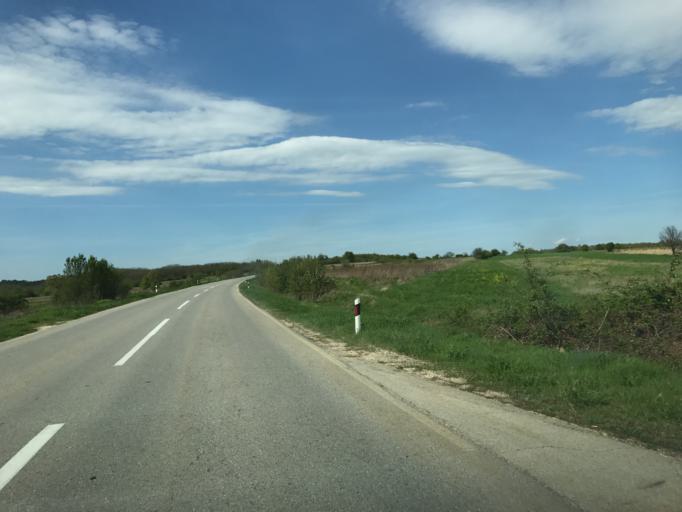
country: RS
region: Central Serbia
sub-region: Zajecarski Okrug
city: Zajecar
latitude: 44.0460
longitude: 22.3344
